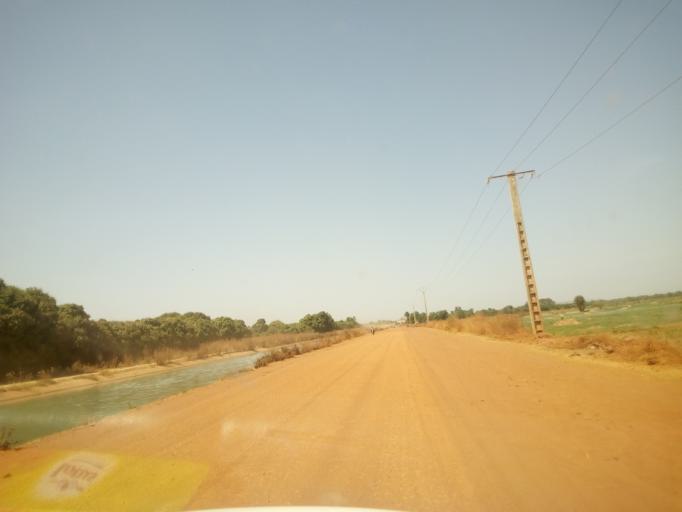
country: ML
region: Bamako
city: Bamako
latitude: 12.6209
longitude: -7.7659
